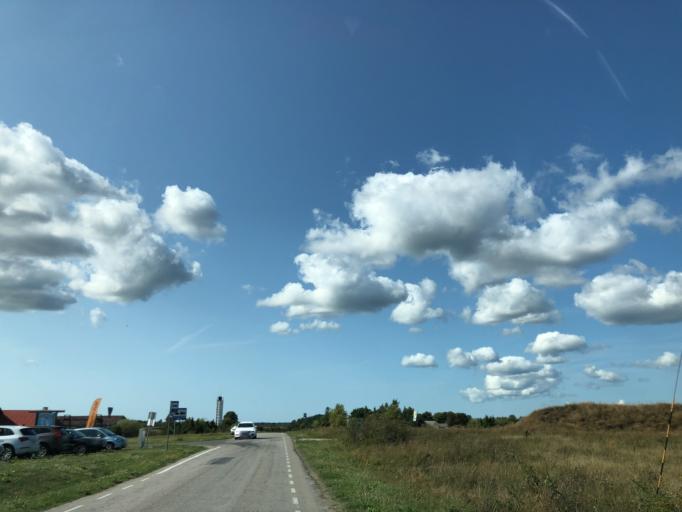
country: EE
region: Hiiumaa
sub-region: Kaerdla linn
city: Kardla
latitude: 58.7891
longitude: 22.7738
